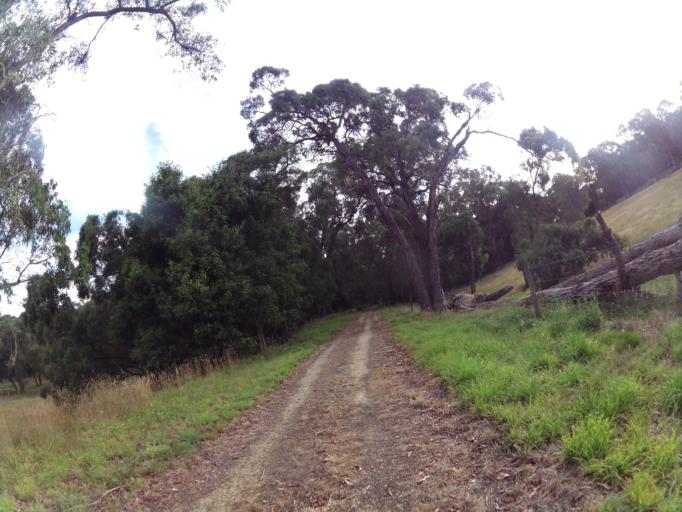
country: AU
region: Victoria
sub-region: Colac-Otway
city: Colac
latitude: -38.5017
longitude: 143.7269
